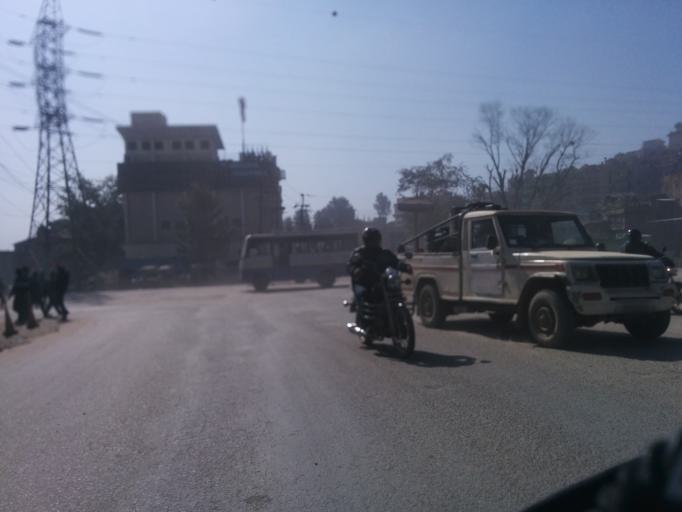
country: NP
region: Central Region
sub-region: Bagmati Zone
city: Patan
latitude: 27.6852
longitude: 85.2983
